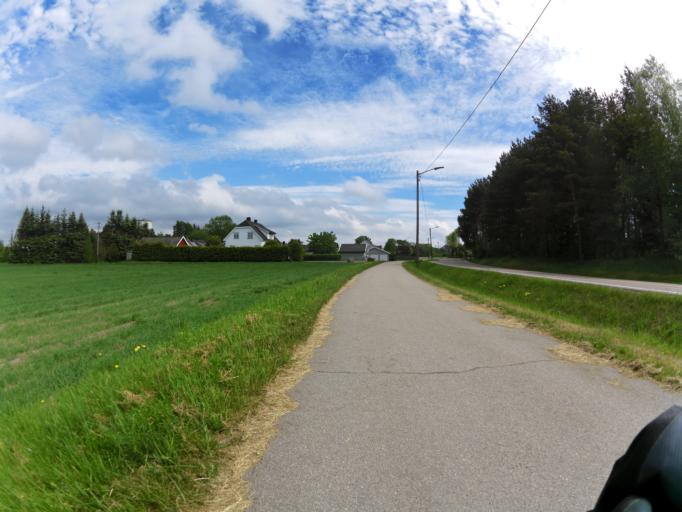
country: NO
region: Ostfold
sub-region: Rade
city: Karlshus
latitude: 59.3491
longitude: 10.8865
